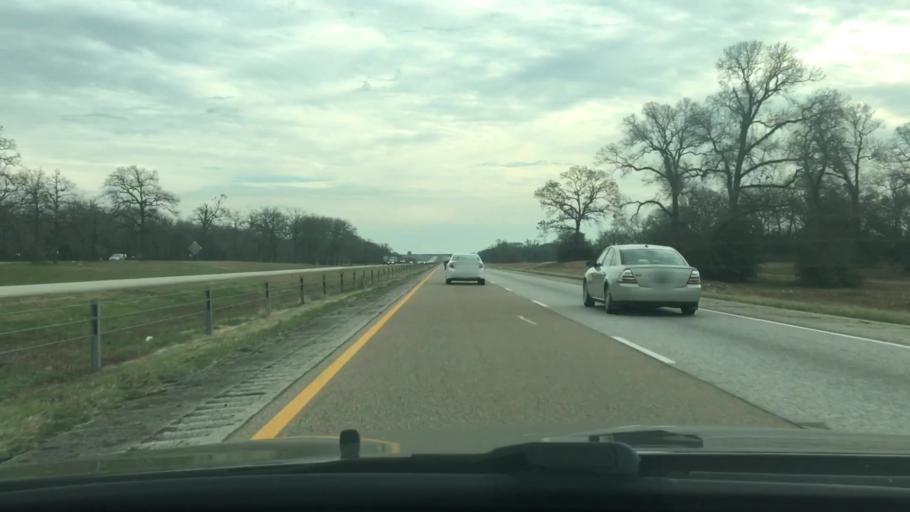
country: US
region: Texas
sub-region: Leon County
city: Centerville
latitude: 31.1384
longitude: -95.9802
